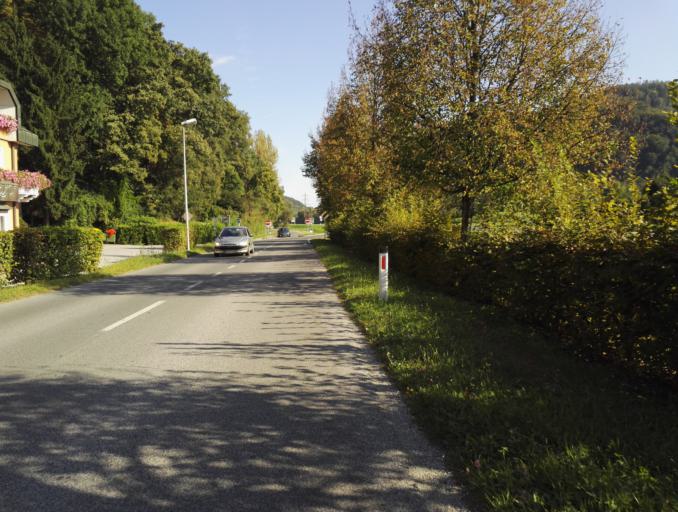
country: AT
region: Styria
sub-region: Politischer Bezirk Graz-Umgebung
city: Gratkorn
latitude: 47.1235
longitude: 15.3547
